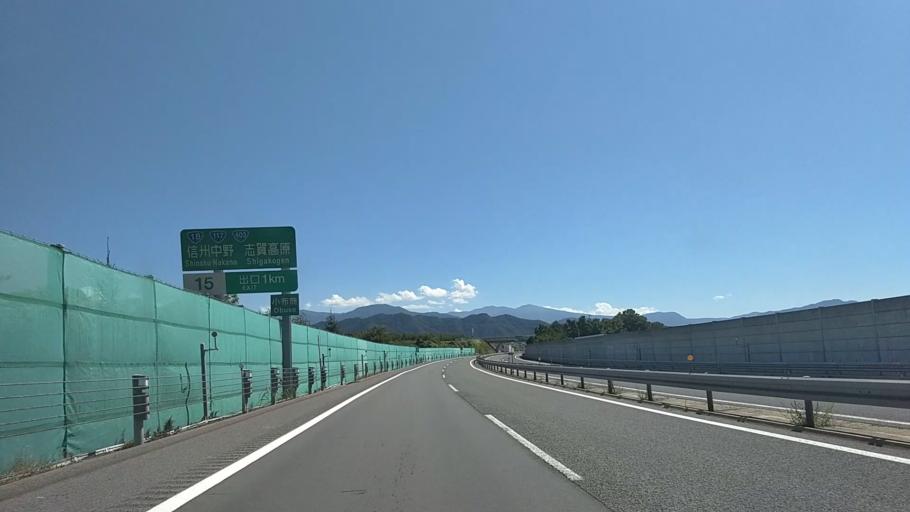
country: JP
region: Nagano
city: Nakano
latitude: 36.7407
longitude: 138.3161
